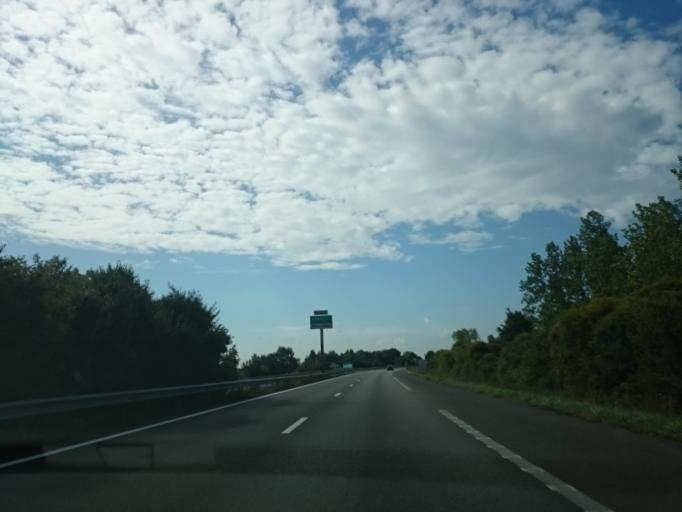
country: FR
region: Pays de la Loire
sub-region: Departement de la Loire-Atlantique
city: Heric
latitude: 47.4255
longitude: -1.6381
